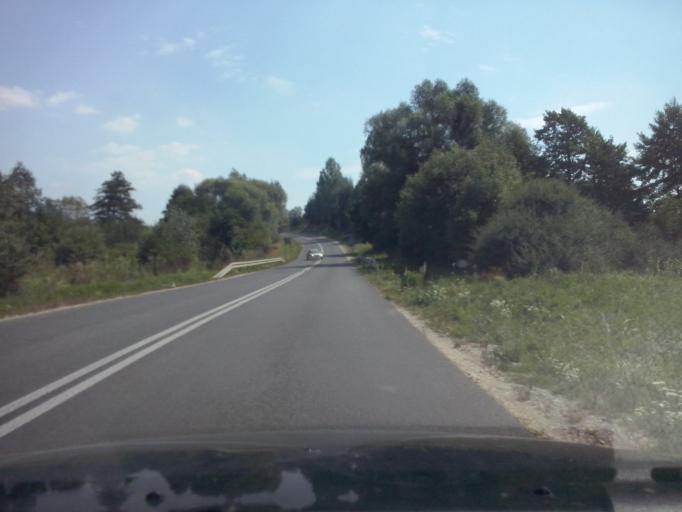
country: PL
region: Swietokrzyskie
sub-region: Powiat buski
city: Gnojno
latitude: 50.6073
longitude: 20.8171
